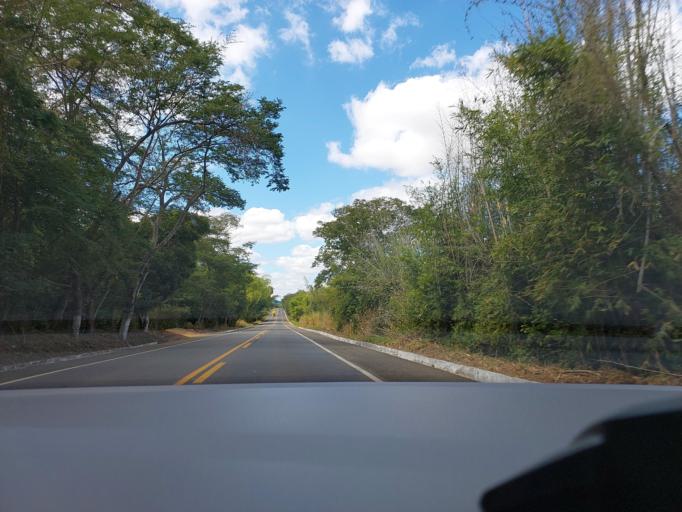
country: BR
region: Minas Gerais
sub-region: Muriae
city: Muriae
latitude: -21.1357
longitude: -42.1846
